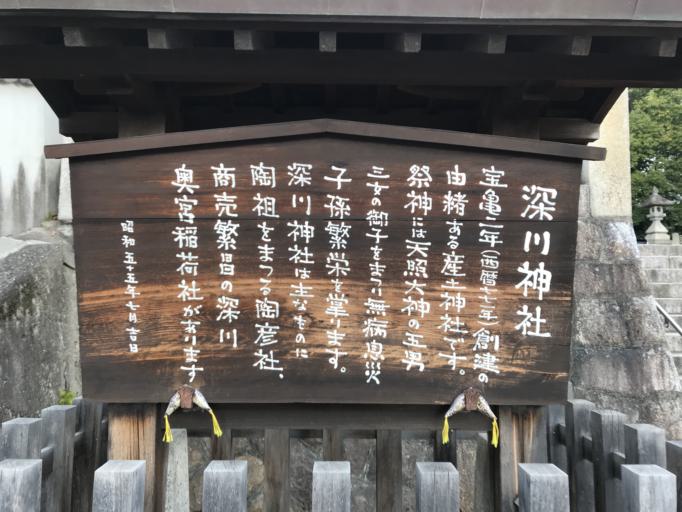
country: JP
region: Aichi
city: Seto
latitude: 35.2275
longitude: 137.1027
